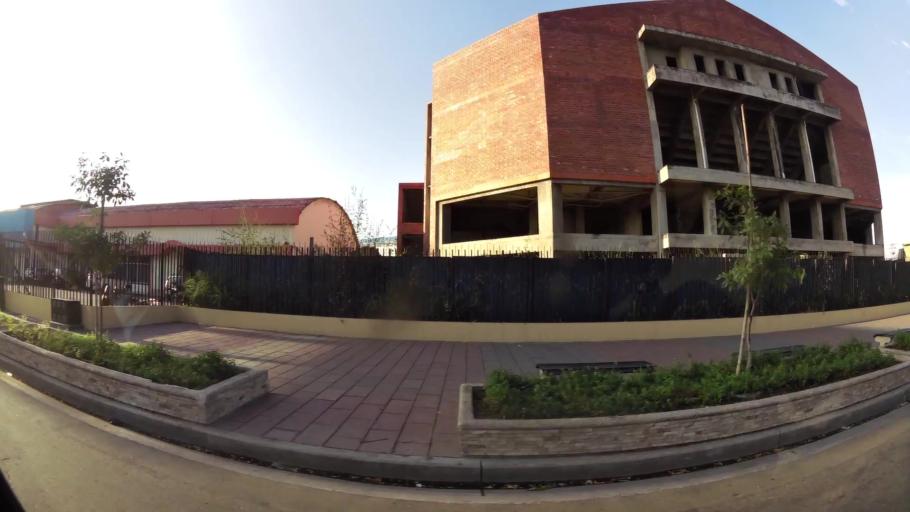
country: EC
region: Guayas
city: Guayaquil
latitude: -2.1804
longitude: -79.8952
